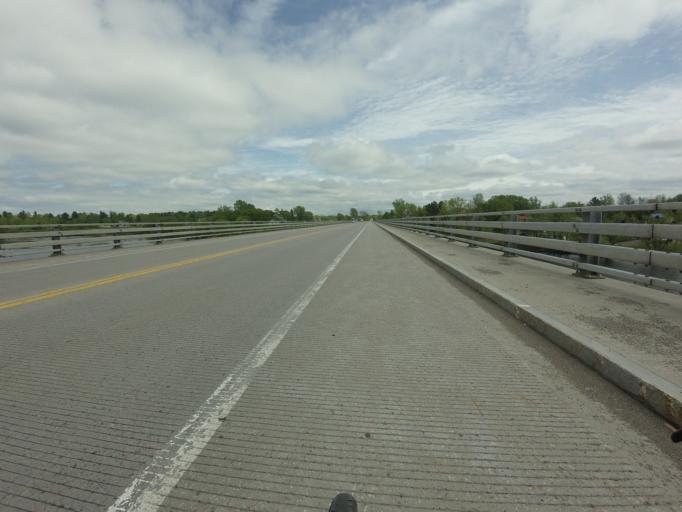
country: CA
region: Ontario
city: Cornwall
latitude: 44.9788
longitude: -74.7180
